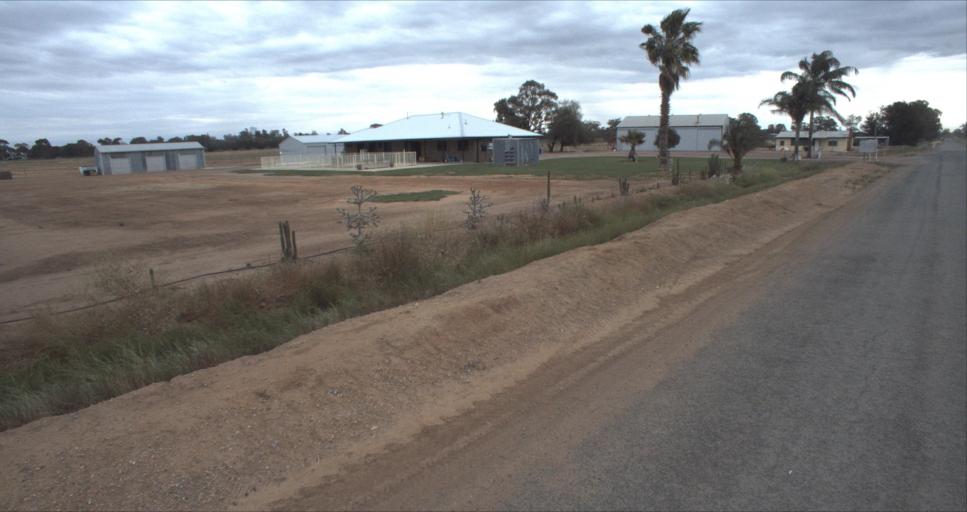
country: AU
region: New South Wales
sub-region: Leeton
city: Leeton
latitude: -34.5430
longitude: 146.3829
